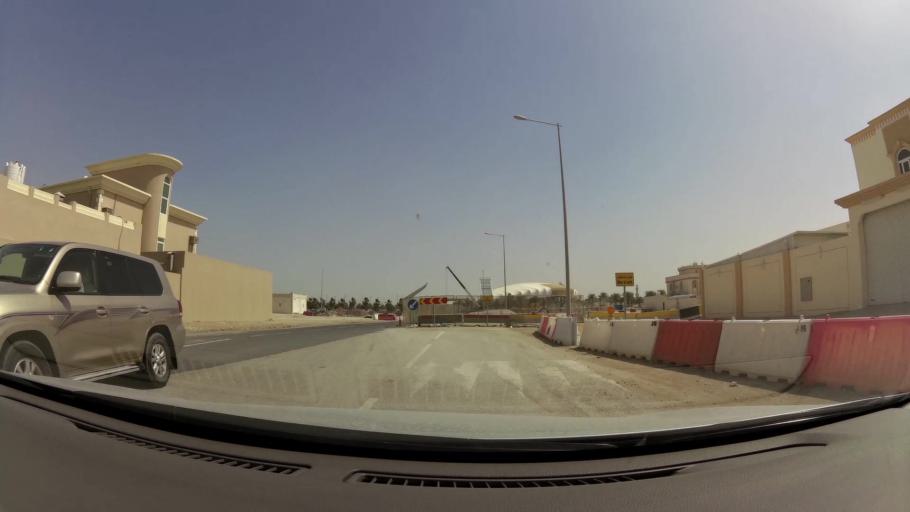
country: QA
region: Baladiyat Umm Salal
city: Umm Salal Muhammad
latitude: 25.3770
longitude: 51.4667
